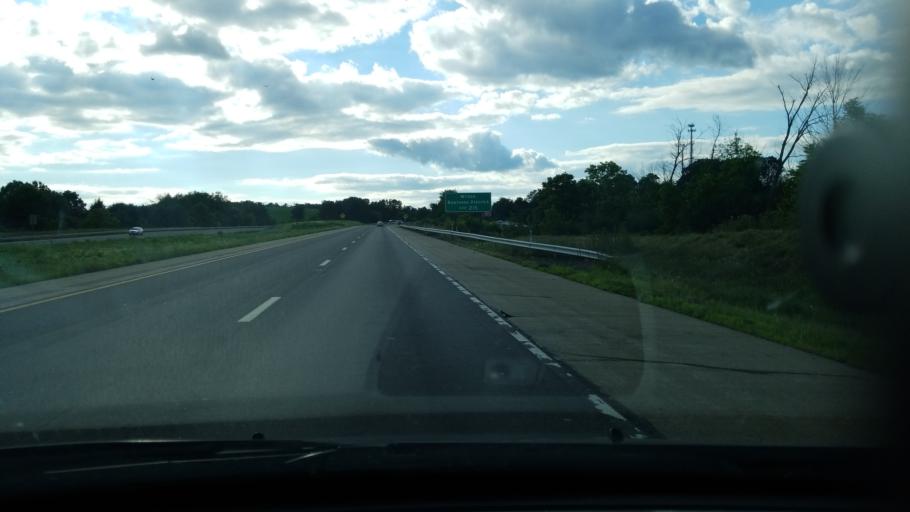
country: US
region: Pennsylvania
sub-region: Northumberland County
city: Milton
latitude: 41.0114
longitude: -76.7797
